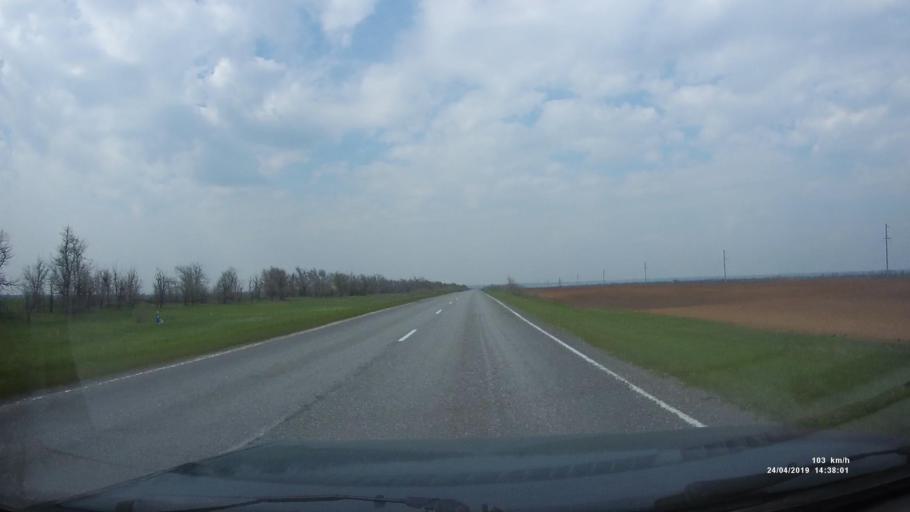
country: RU
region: Rostov
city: Remontnoye
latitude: 46.3948
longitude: 43.8863
